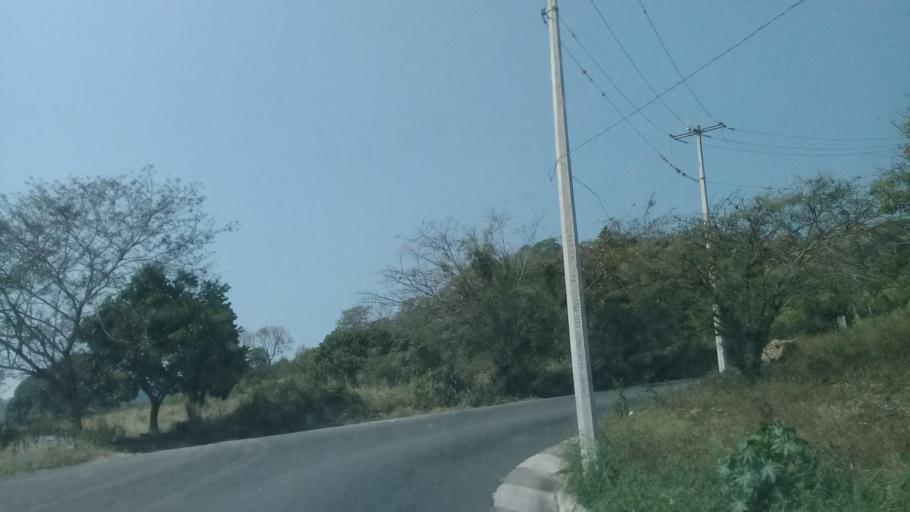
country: MX
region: Veracruz
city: El Castillo
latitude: 19.5688
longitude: -96.8355
